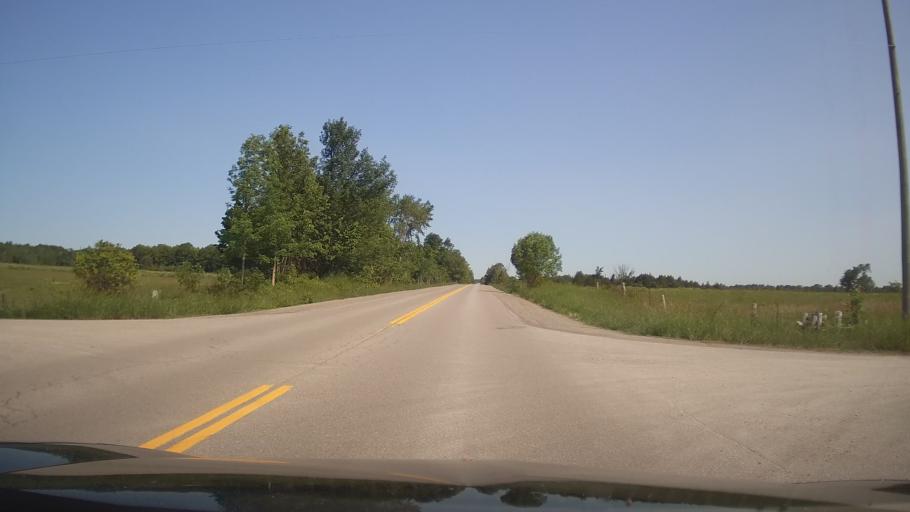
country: CA
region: Ontario
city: Uxbridge
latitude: 44.4975
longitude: -78.9493
